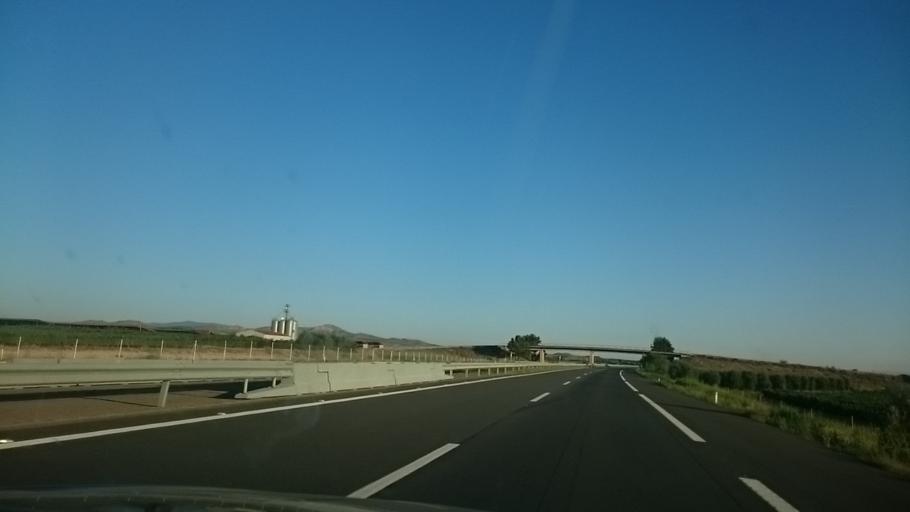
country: ES
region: La Rioja
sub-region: Provincia de La Rioja
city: Aldeanueva de Ebro
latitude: 42.2166
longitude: -1.8891
